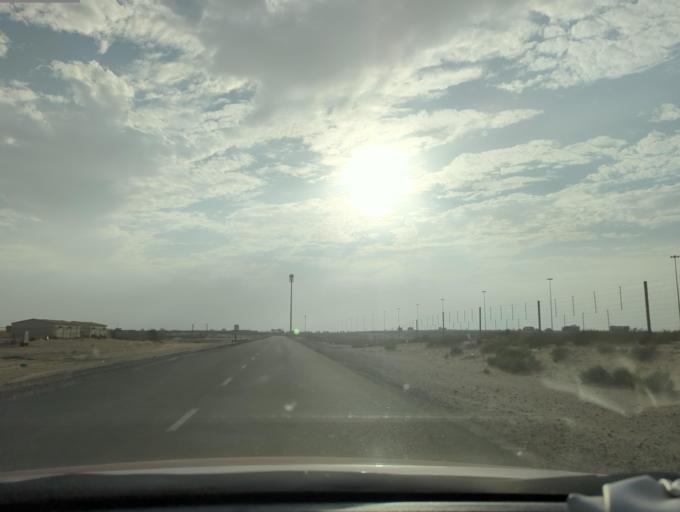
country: AE
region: Dubai
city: Dubai
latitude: 24.7243
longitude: 54.8711
